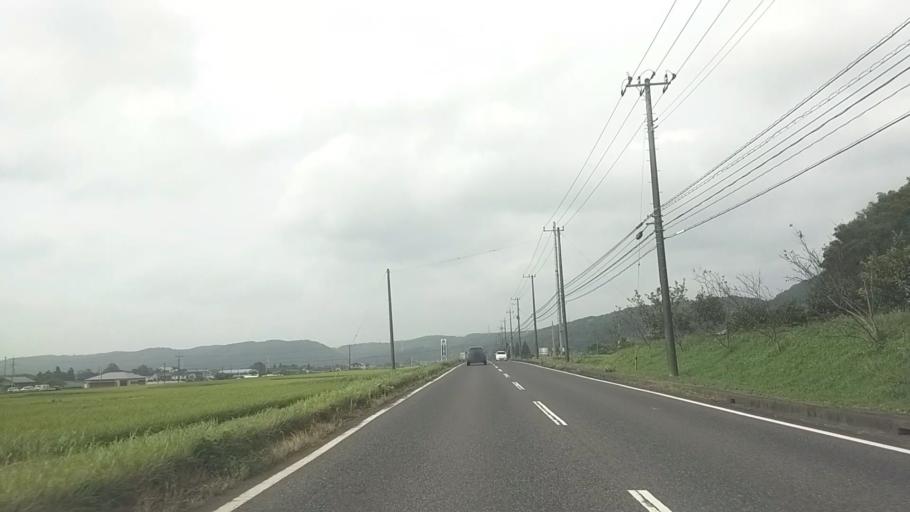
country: JP
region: Chiba
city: Kimitsu
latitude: 35.2844
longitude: 139.9902
